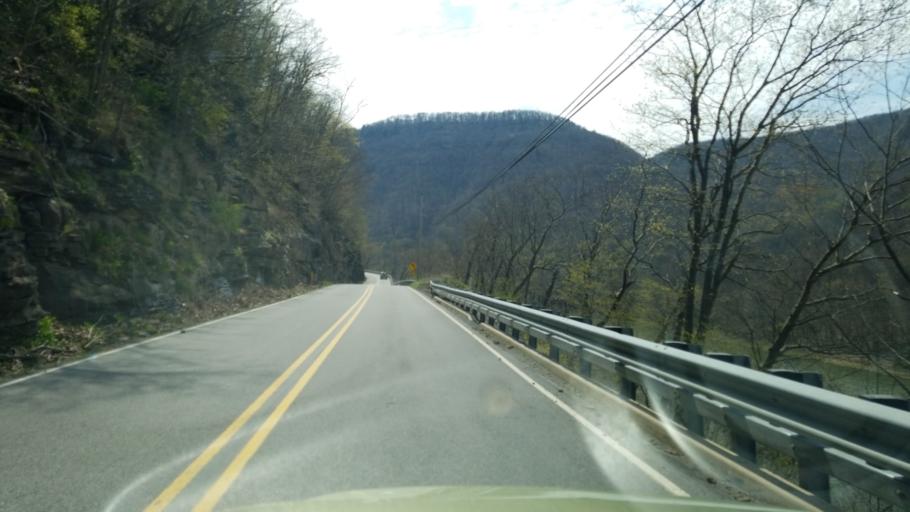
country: US
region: Pennsylvania
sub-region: Clinton County
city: Renovo
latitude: 41.3061
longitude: -77.8150
